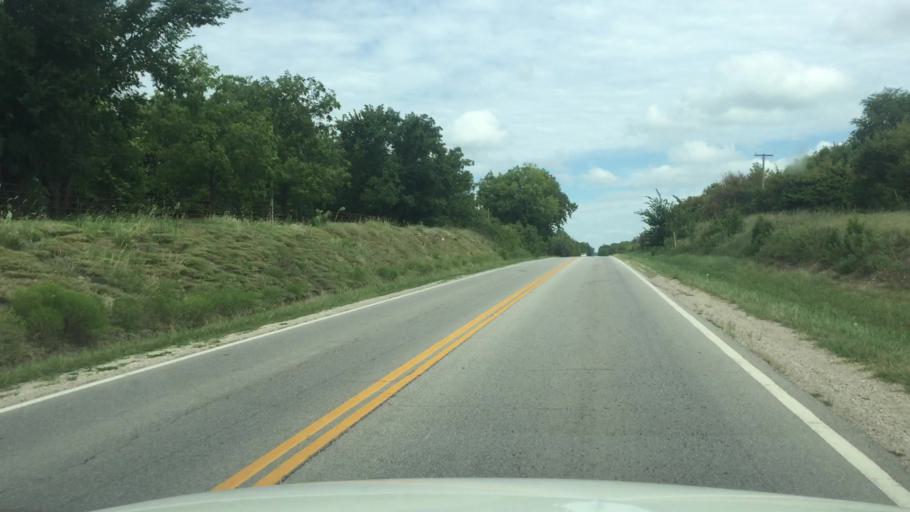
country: US
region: Kansas
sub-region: Anderson County
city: Garnett
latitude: 38.2638
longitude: -95.2490
